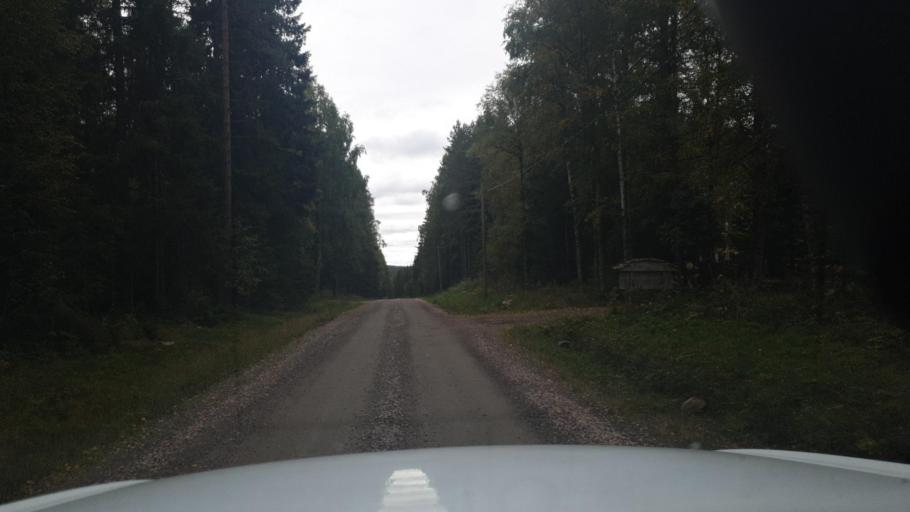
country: SE
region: Vaermland
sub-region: Eda Kommun
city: Charlottenberg
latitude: 60.1526
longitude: 12.5966
